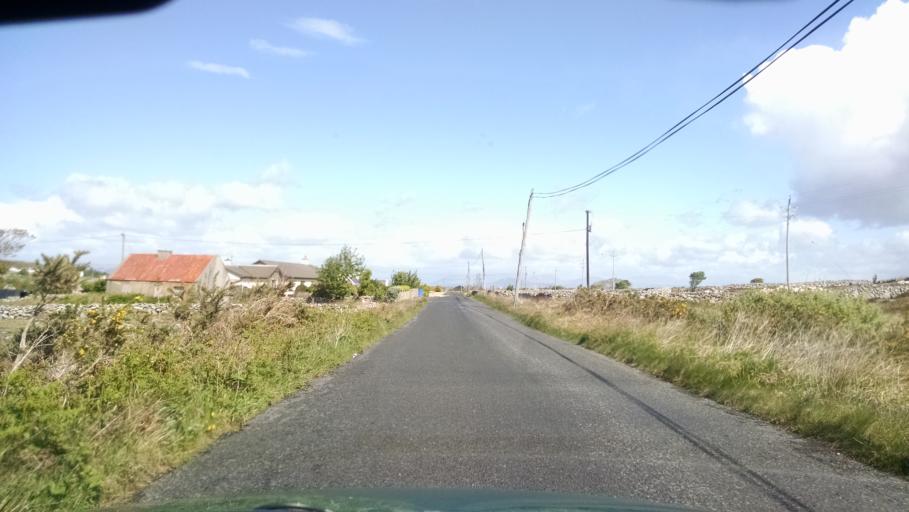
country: IE
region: Connaught
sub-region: County Galway
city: Oughterard
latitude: 53.2567
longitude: -9.5428
